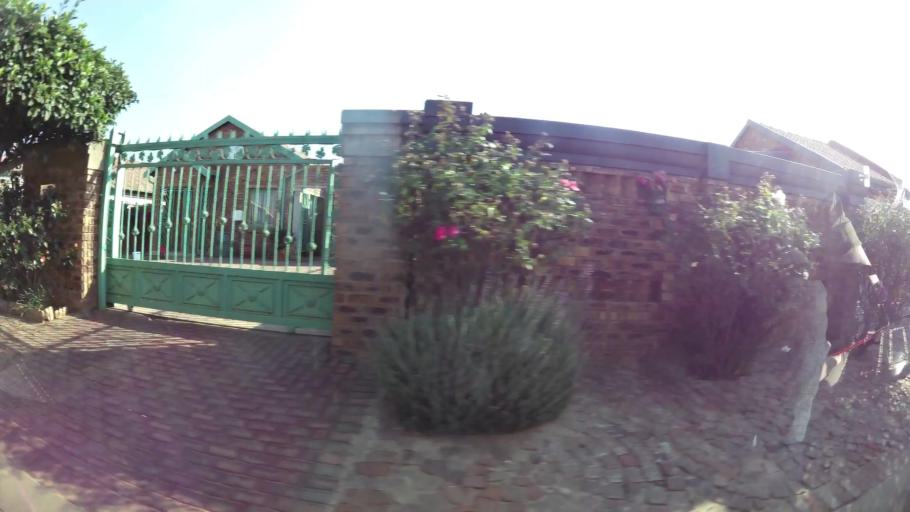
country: ZA
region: Gauteng
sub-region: Ekurhuleni Metropolitan Municipality
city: Benoni
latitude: -26.1567
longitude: 28.3985
